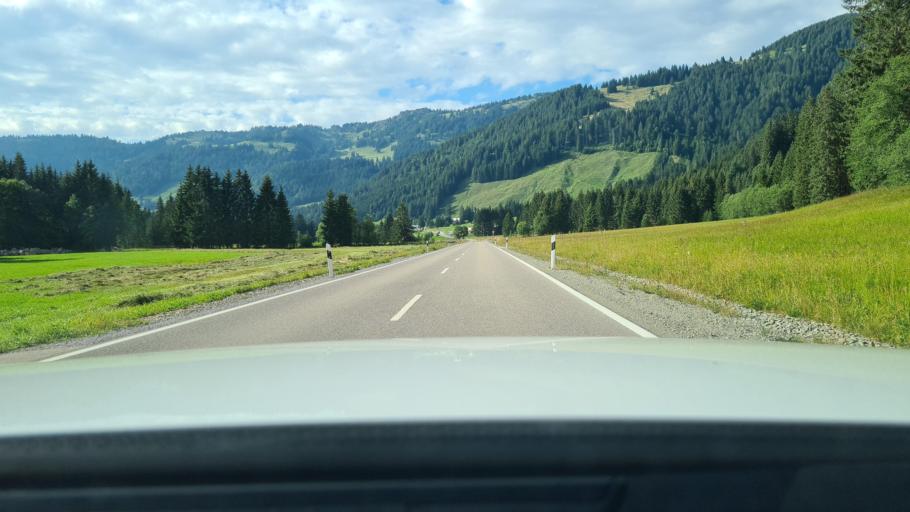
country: DE
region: Bavaria
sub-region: Swabia
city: Balderschwang
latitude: 47.4497
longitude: 10.1338
